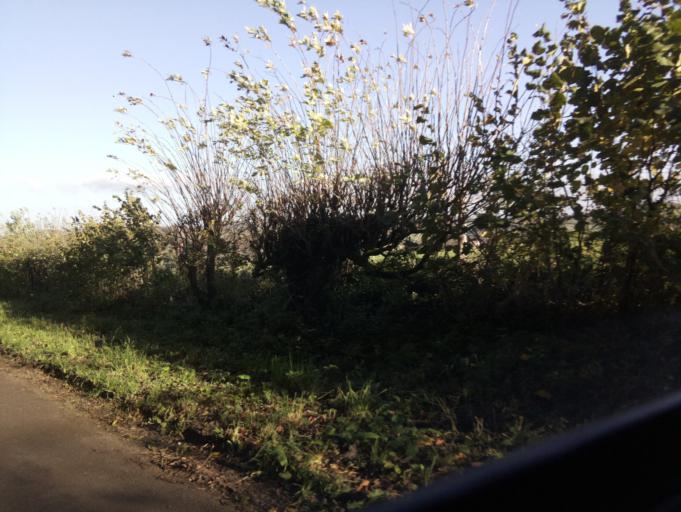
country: GB
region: England
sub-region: Somerset
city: Castle Cary
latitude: 51.0312
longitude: -2.4988
